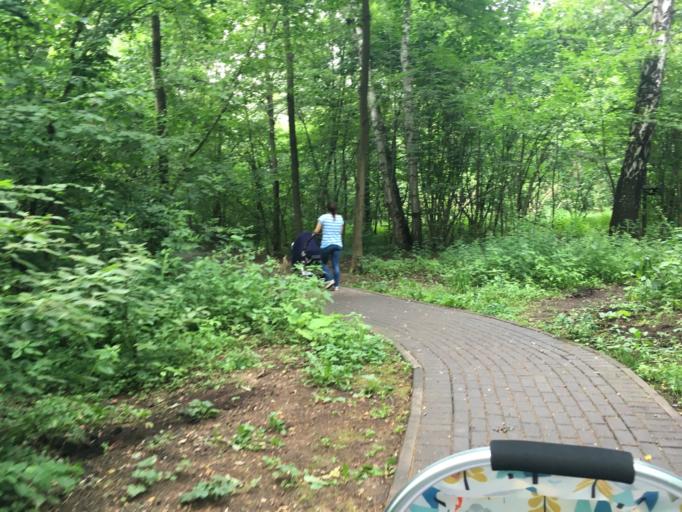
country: RU
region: Moscow
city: Ostankinskiy
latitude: 55.8300
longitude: 37.6045
